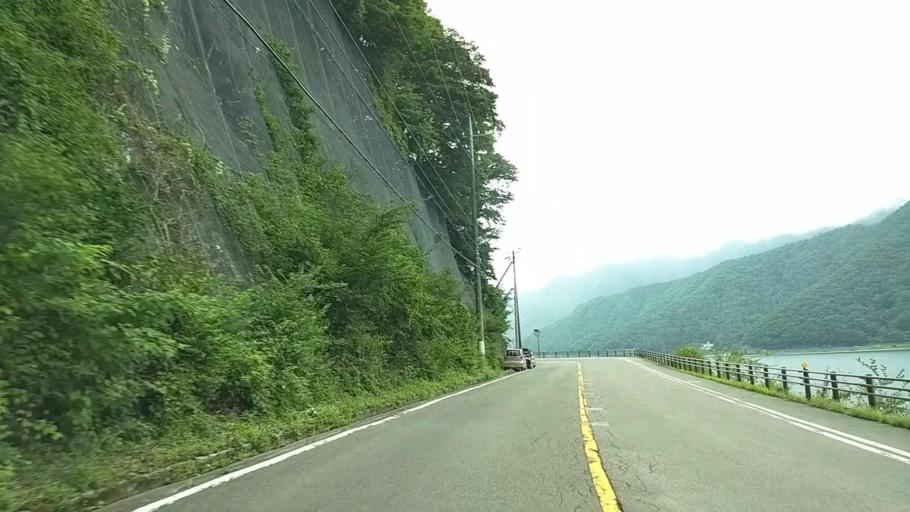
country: JP
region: Yamanashi
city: Fujikawaguchiko
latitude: 35.4951
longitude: 138.6890
